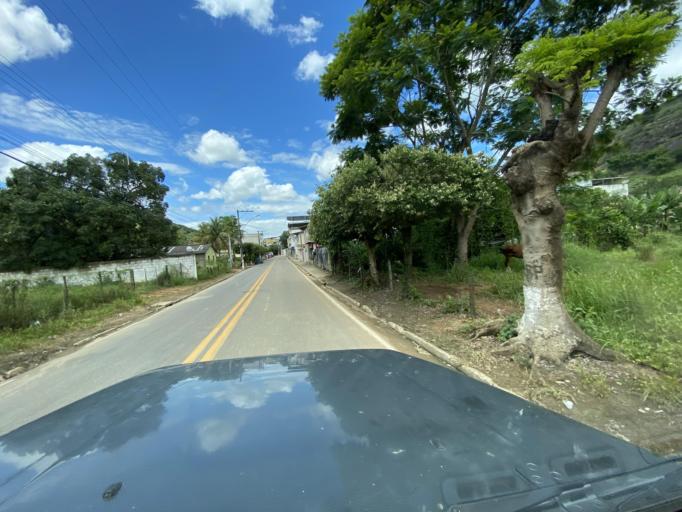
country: BR
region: Espirito Santo
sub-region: Jeronimo Monteiro
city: Jeronimo Monteiro
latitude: -20.7949
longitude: -41.4019
